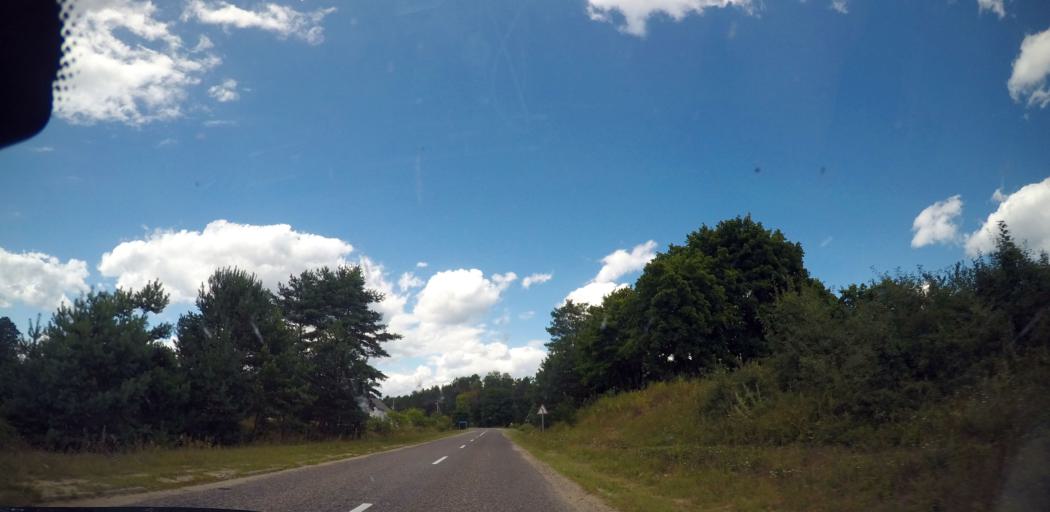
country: BY
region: Grodnenskaya
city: Skidal'
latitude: 53.8220
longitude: 24.2422
